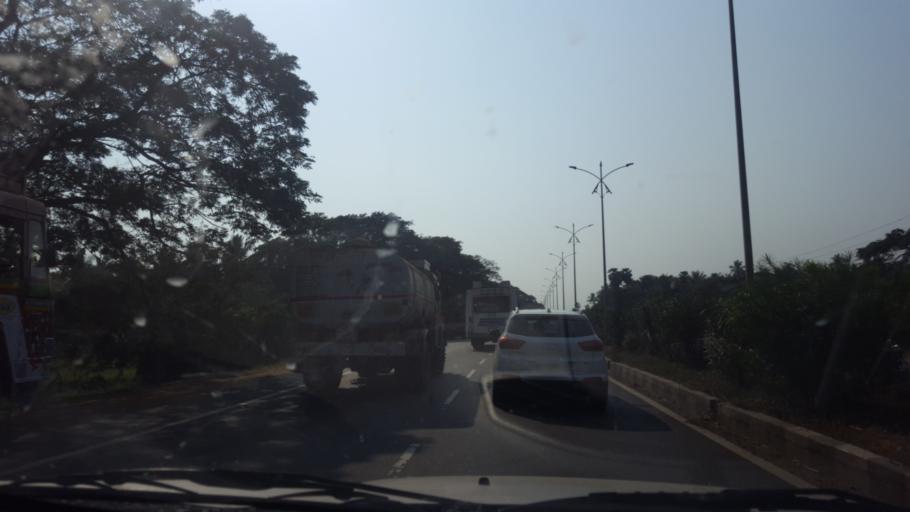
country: IN
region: Andhra Pradesh
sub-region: Vishakhapatnam
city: Anakapalle
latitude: 17.6768
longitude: 83.0222
